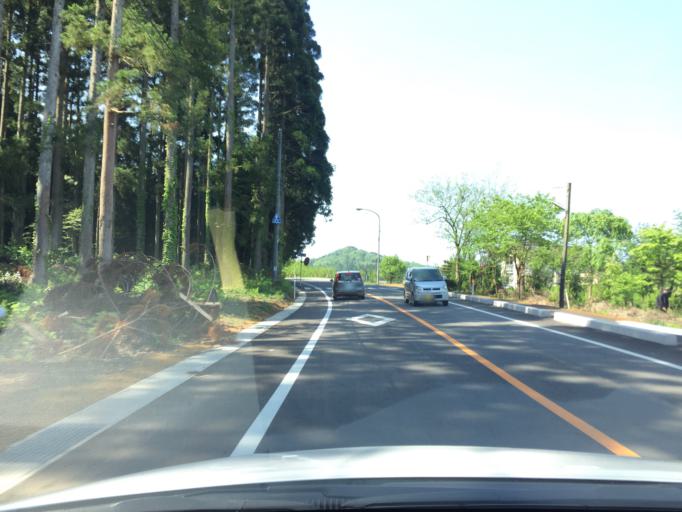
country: JP
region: Niigata
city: Muramatsu
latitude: 37.6649
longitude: 139.1389
